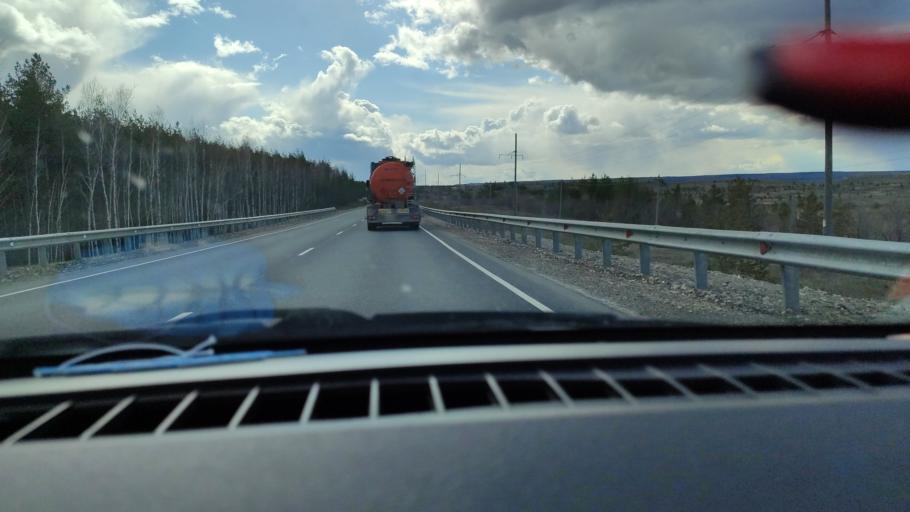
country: RU
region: Saratov
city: Khvalynsk
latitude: 52.5383
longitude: 48.0479
